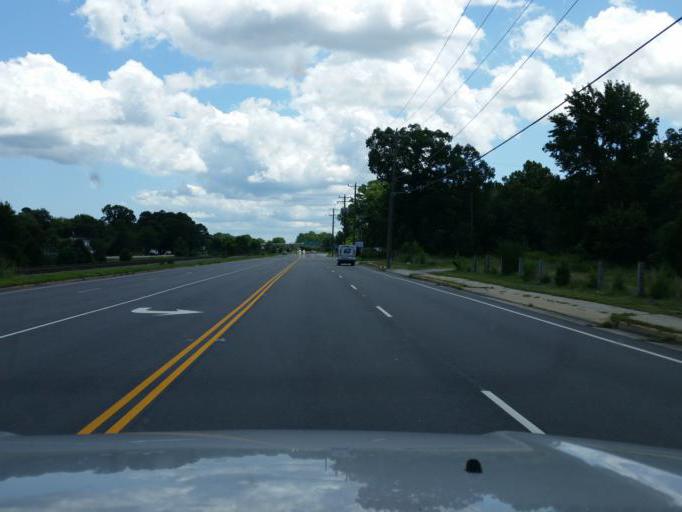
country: US
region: Virginia
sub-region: City of Williamsburg
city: Williamsburg
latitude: 37.2567
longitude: -76.6692
